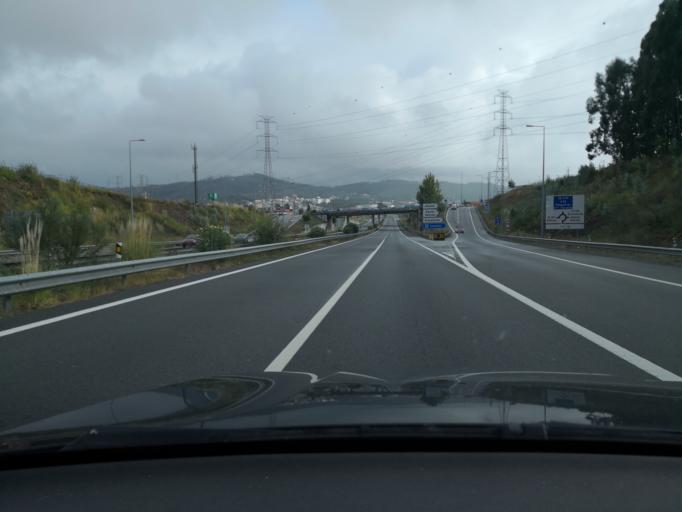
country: PT
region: Porto
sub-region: Valongo
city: Alfena
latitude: 41.2362
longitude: -8.5428
